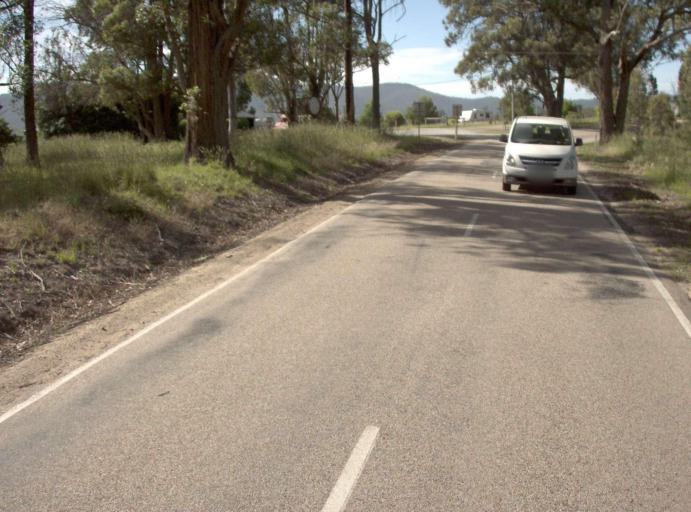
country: AU
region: Victoria
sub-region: East Gippsland
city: Lakes Entrance
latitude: -37.5200
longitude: 148.1623
